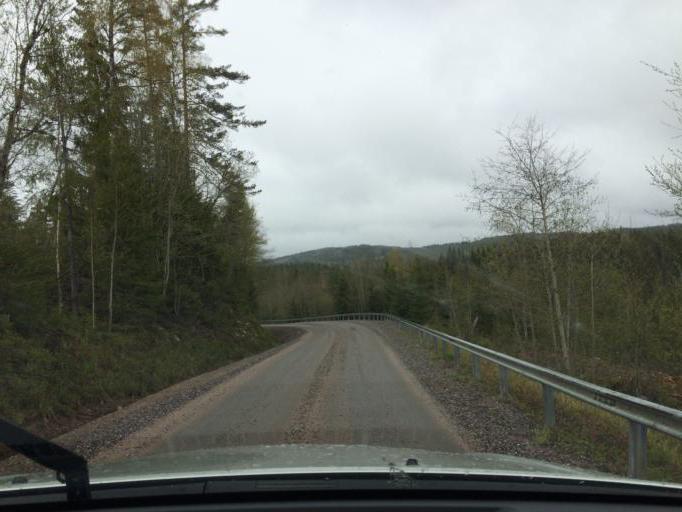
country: SE
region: Dalarna
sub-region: Ludvika Kommun
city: Abborrberget
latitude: 60.0209
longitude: 14.6048
